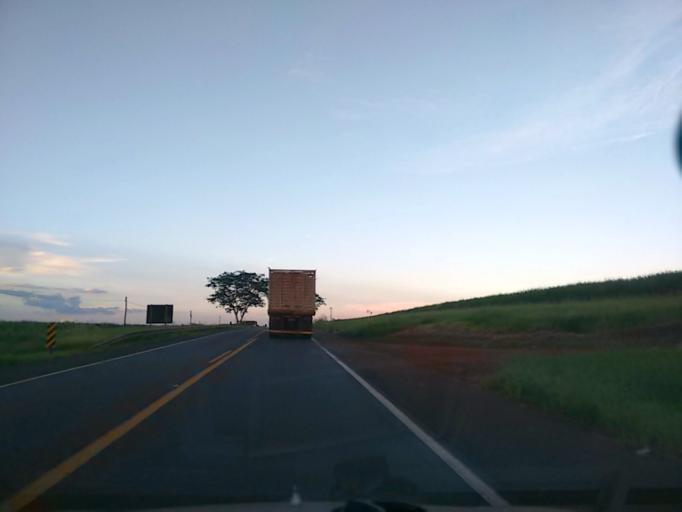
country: BR
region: Sao Paulo
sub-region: Boa Esperanca Do Sul
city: Boa Esperanca do Sul
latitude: -22.1277
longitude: -48.4587
